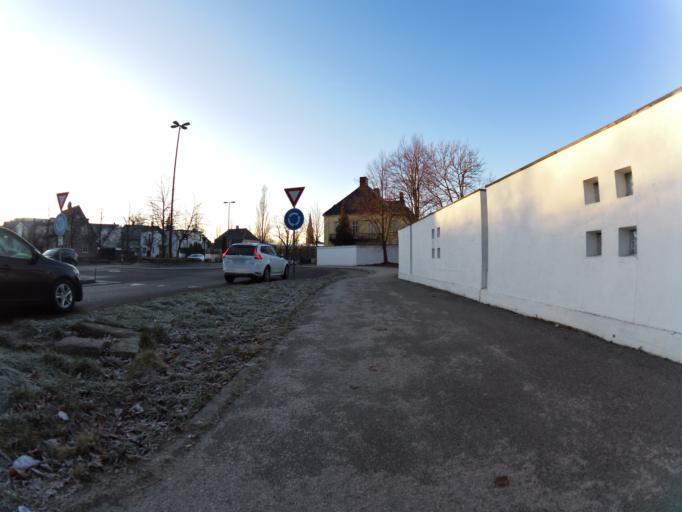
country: NO
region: Ostfold
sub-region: Fredrikstad
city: Fredrikstad
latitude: 59.2104
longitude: 10.9499
